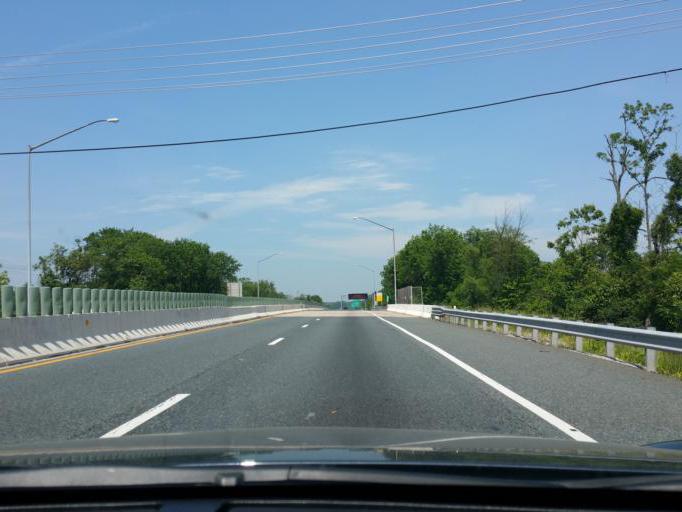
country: US
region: Maryland
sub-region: Baltimore County
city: Baltimore Highlands
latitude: 39.2294
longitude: -76.6350
